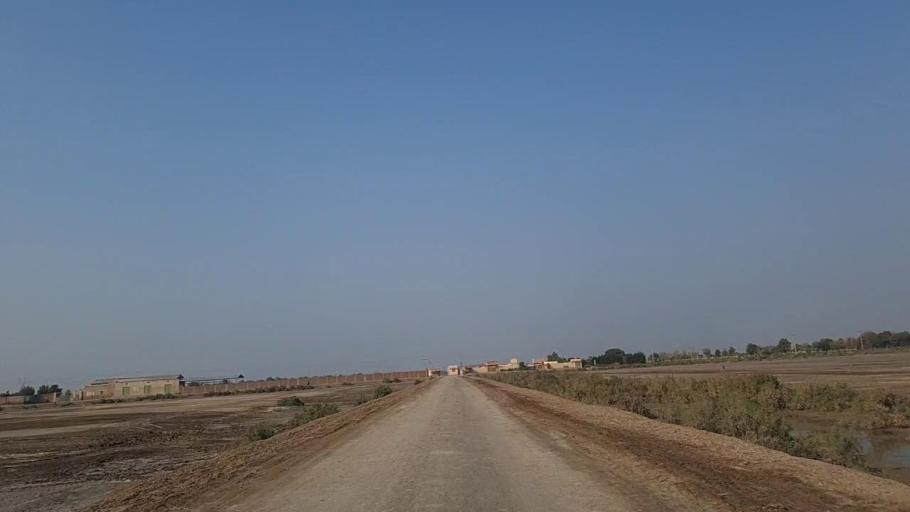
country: PK
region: Sindh
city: Jam Sahib
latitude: 26.2877
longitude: 68.6086
